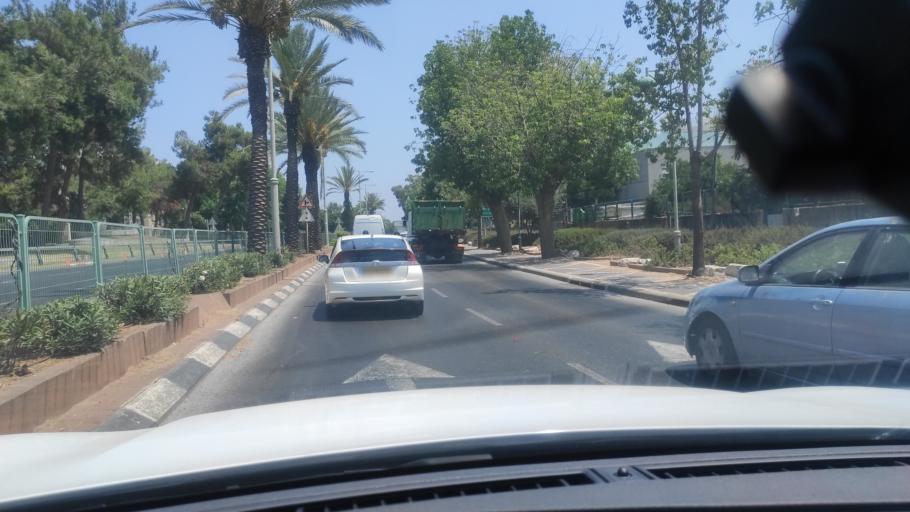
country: IL
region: Central District
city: Petah Tiqwa
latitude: 32.0888
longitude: 34.9016
